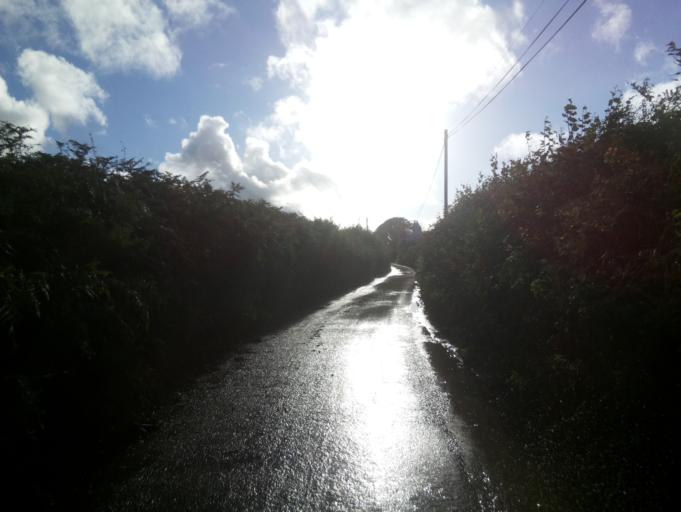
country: GB
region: England
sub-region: Devon
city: Dartmouth
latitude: 50.3453
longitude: -3.6545
